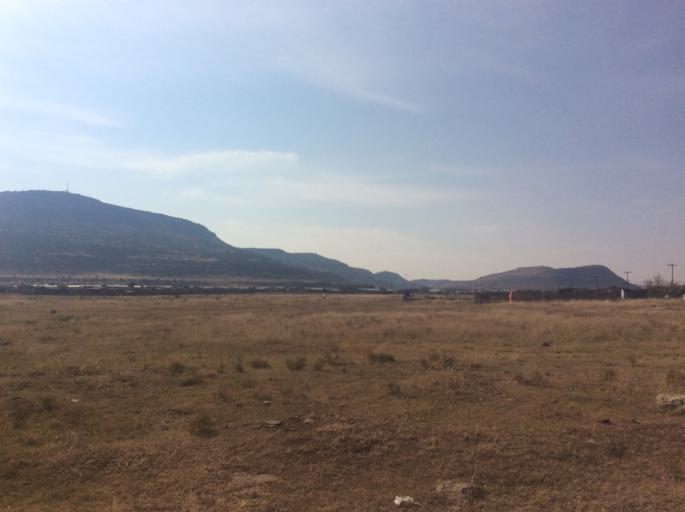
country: LS
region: Mafeteng
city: Mafeteng
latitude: -29.7138
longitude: 27.0101
